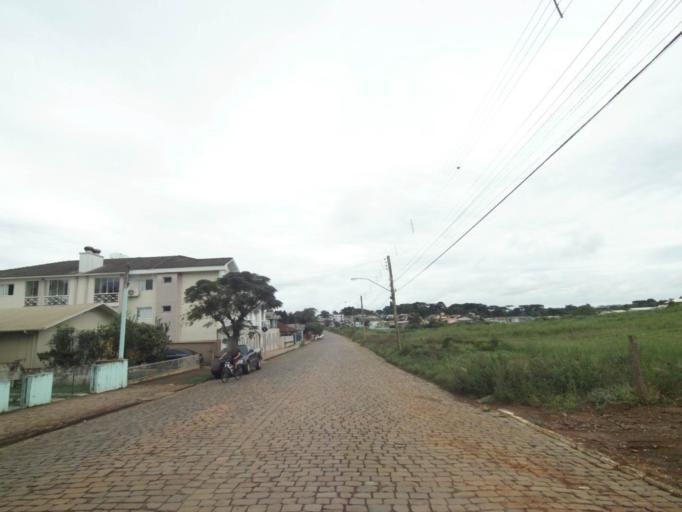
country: BR
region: Rio Grande do Sul
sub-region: Lagoa Vermelha
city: Lagoa Vermelha
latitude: -28.2142
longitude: -51.5220
